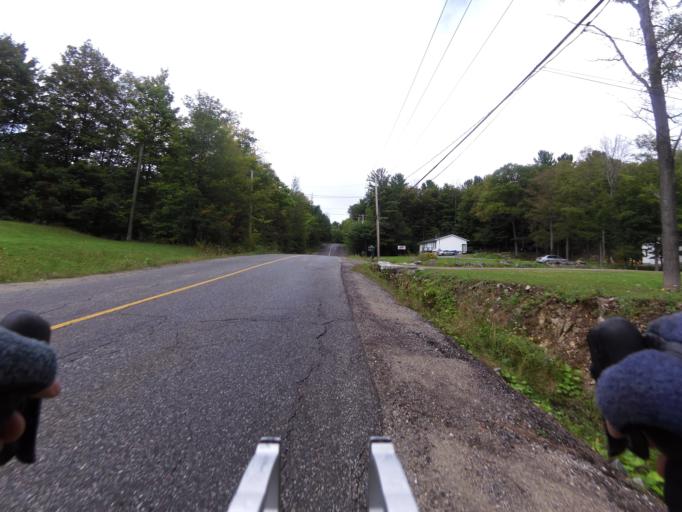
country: CA
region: Quebec
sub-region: Outaouais
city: Gatineau
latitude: 45.5445
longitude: -75.7427
